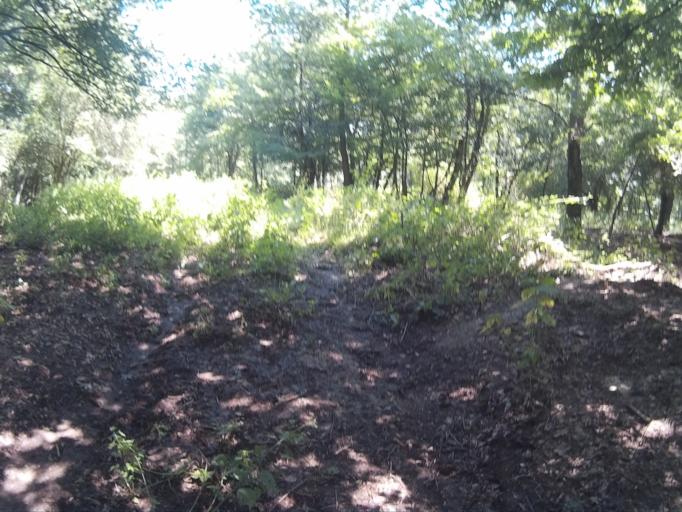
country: HU
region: Veszprem
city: Zirc
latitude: 47.1953
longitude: 17.8860
